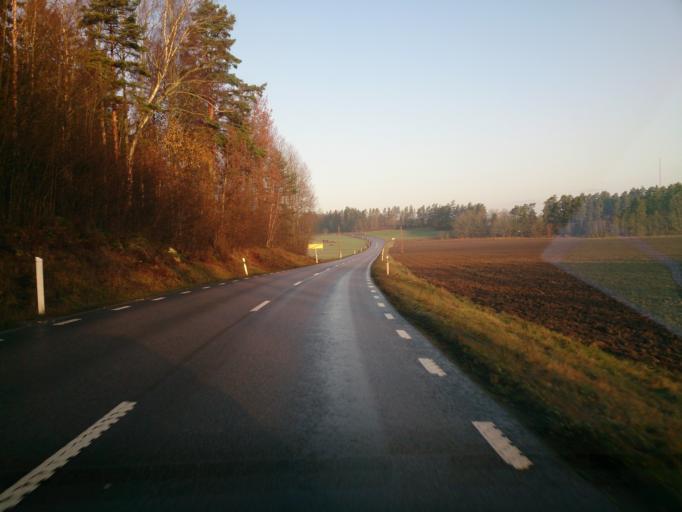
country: SE
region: OEstergoetland
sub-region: Atvidabergs Kommun
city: Atvidaberg
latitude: 58.2552
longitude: 15.9295
